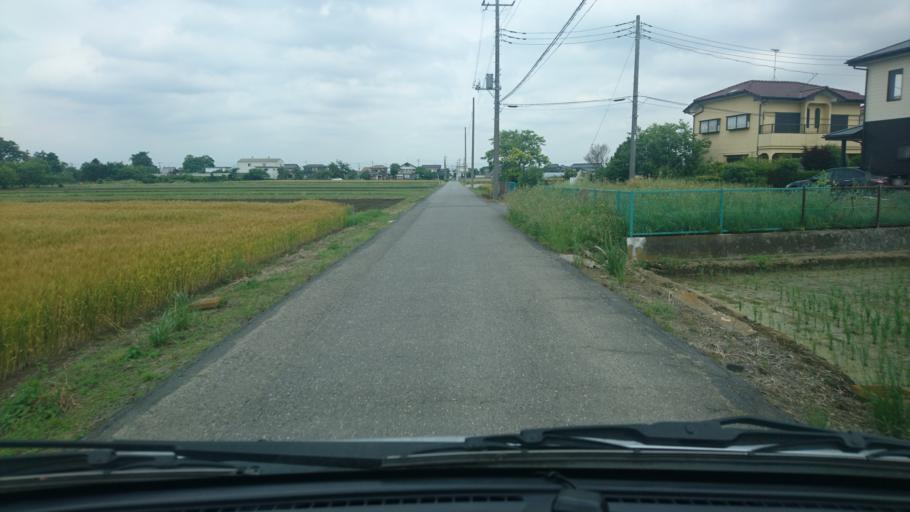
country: JP
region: Ibaraki
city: Ishige
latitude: 36.0994
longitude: 139.9790
